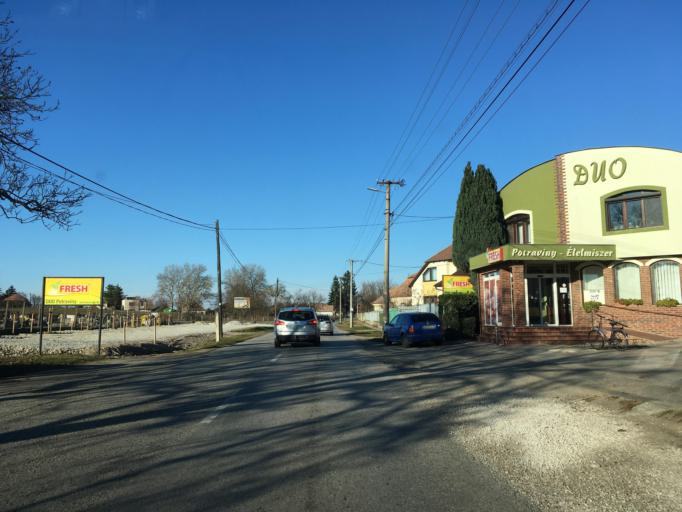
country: SK
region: Nitriansky
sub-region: Okres Komarno
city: Hurbanovo
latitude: 47.9064
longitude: 18.1357
